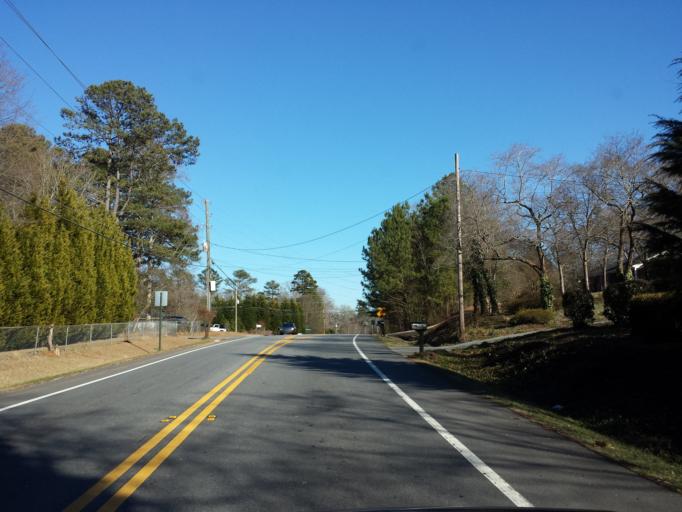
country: US
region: Georgia
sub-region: Cobb County
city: Kennesaw
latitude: 33.9650
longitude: -84.6190
